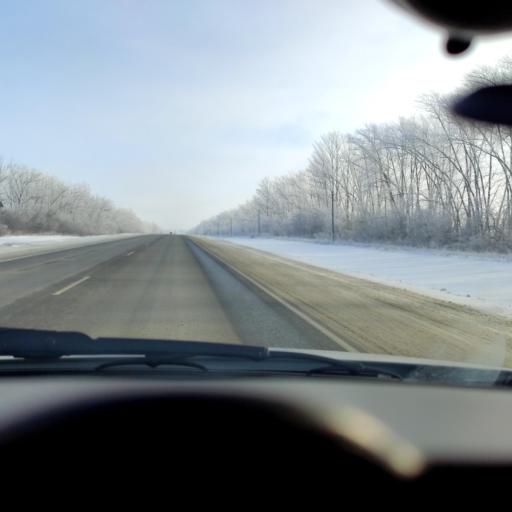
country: RU
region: Belgorod
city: Troitskiy
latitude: 51.6186
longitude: 37.5440
